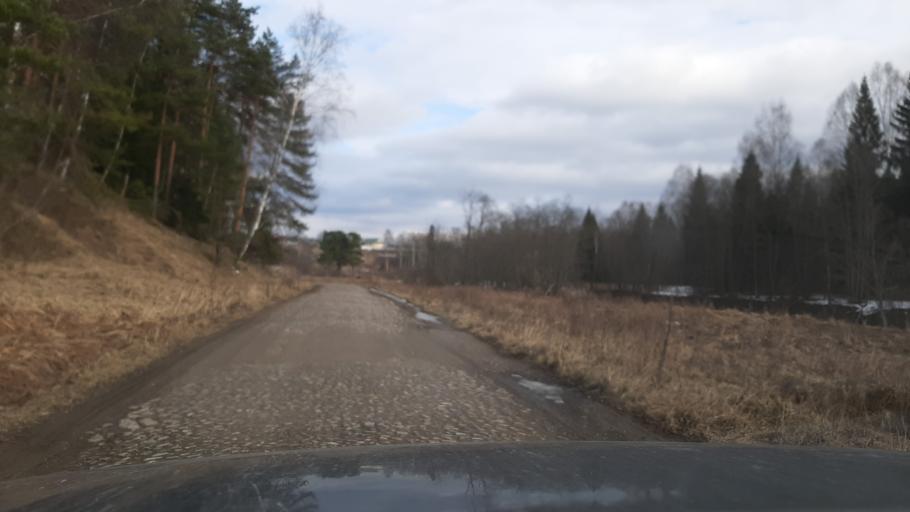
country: RU
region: Ivanovo
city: Teykovo
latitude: 56.8962
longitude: 40.6710
